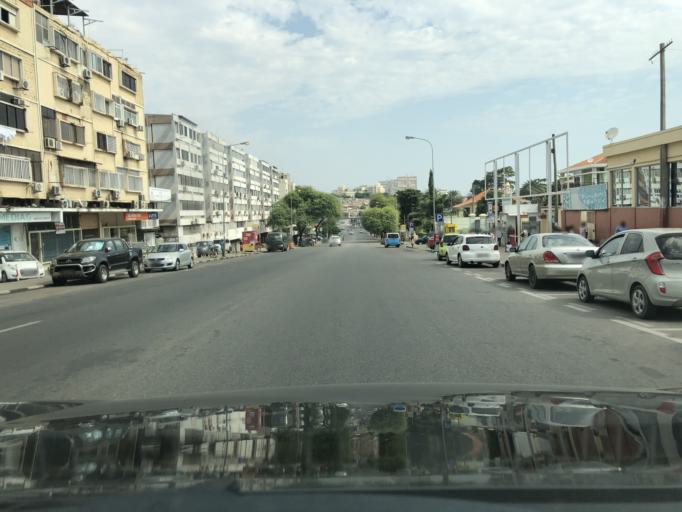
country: AO
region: Luanda
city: Luanda
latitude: -8.8262
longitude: 13.2275
